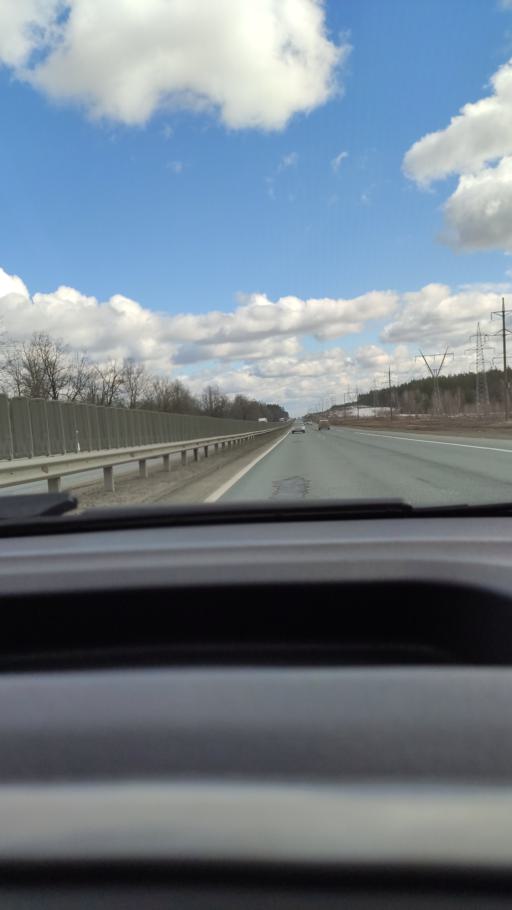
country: RU
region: Samara
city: Pribrezhnyy
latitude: 53.5148
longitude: 49.8745
